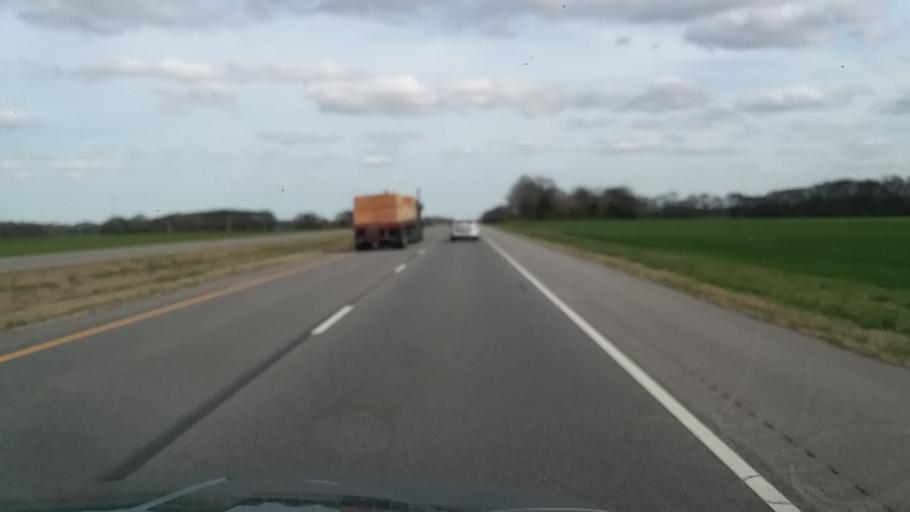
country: US
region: Alabama
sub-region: Lawrence County
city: Town Creek
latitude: 34.6840
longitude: -87.5359
